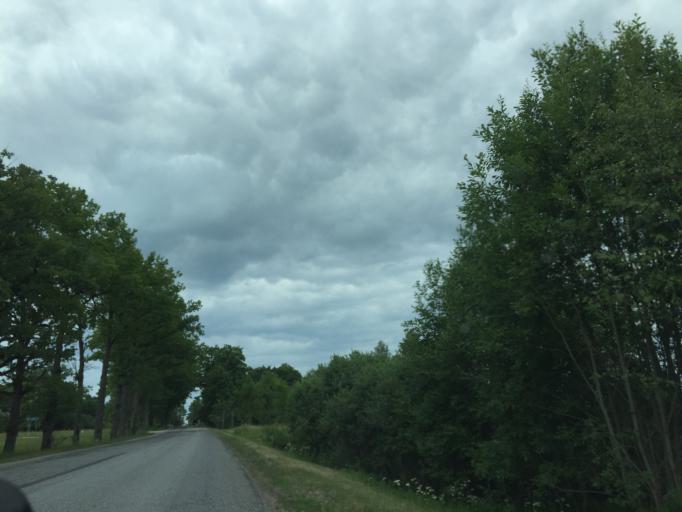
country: LV
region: Skriveri
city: Skriveri
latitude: 56.8322
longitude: 25.1298
